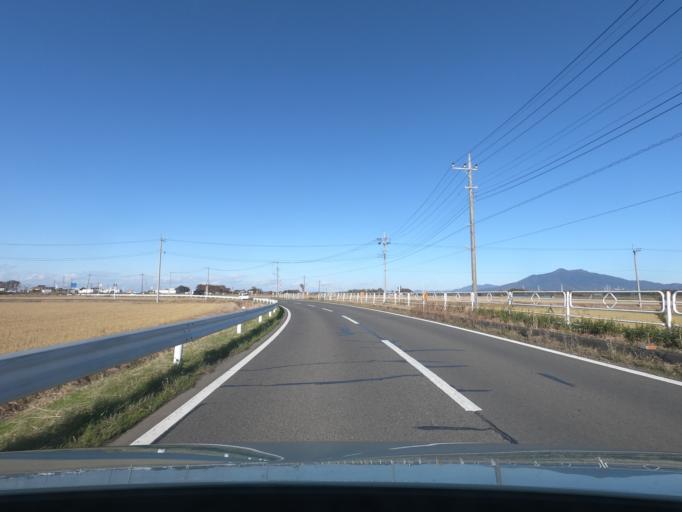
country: JP
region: Ibaraki
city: Ishige
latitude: 36.1557
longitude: 139.9972
